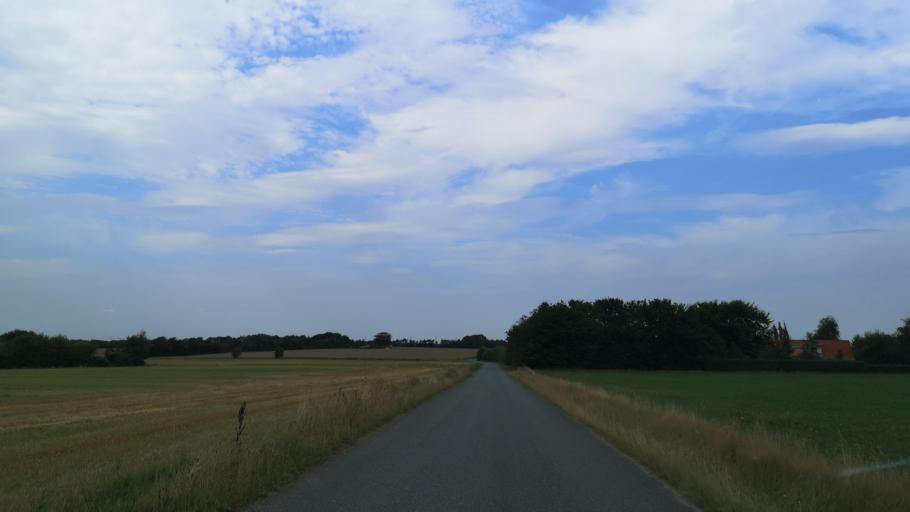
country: DK
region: Central Jutland
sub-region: Ringkobing-Skjern Kommune
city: Videbaek
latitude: 56.0680
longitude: 8.6796
